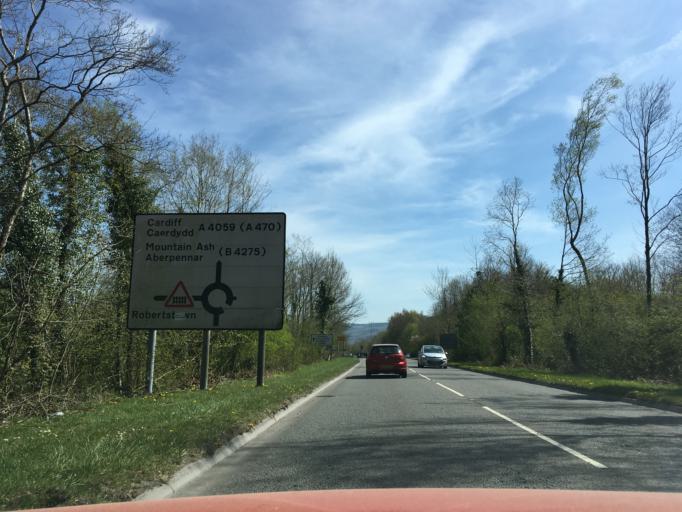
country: GB
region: Wales
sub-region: Rhondda Cynon Taf
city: Aberdare
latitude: 51.7232
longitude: -3.4537
